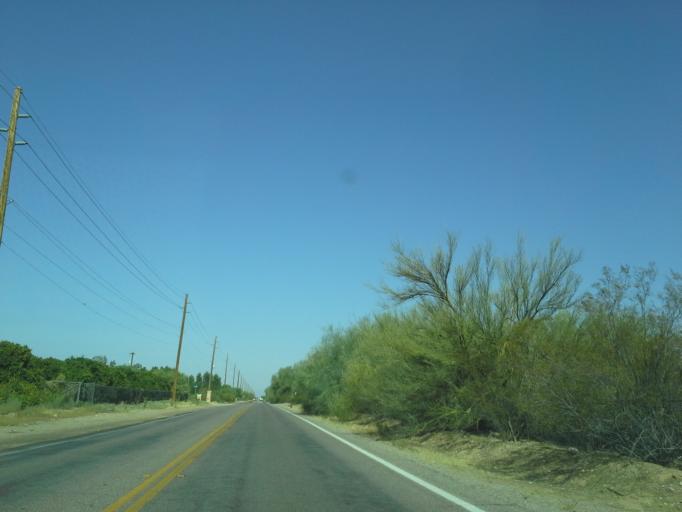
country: US
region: Arizona
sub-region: Maricopa County
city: Queen Creek
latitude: 33.2046
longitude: -111.6835
